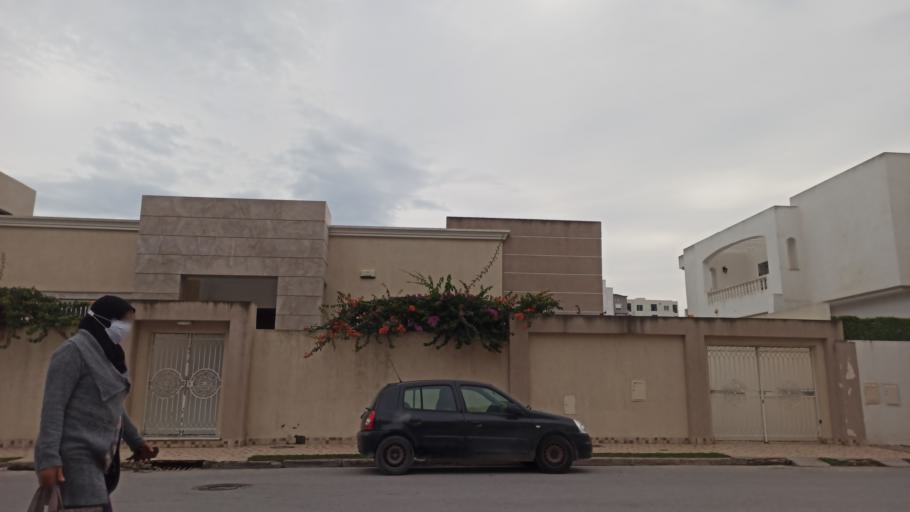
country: TN
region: Tunis
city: La Goulette
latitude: 36.8579
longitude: 10.2650
